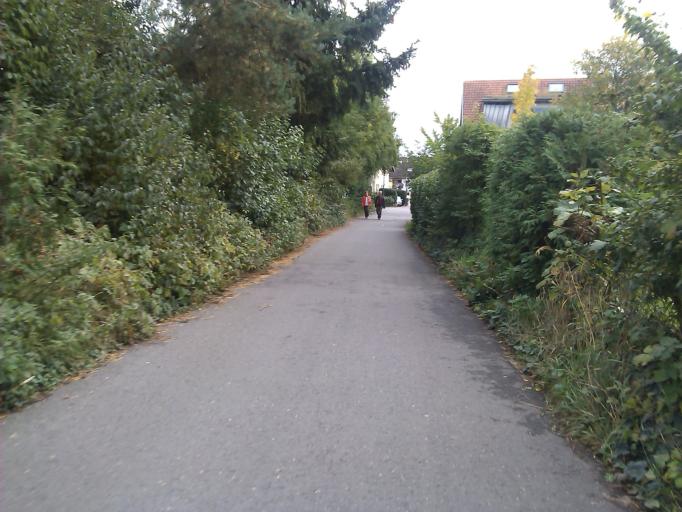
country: DE
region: Baden-Wuerttemberg
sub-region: Karlsruhe Region
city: Dossenheim
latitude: 49.4352
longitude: 8.6829
